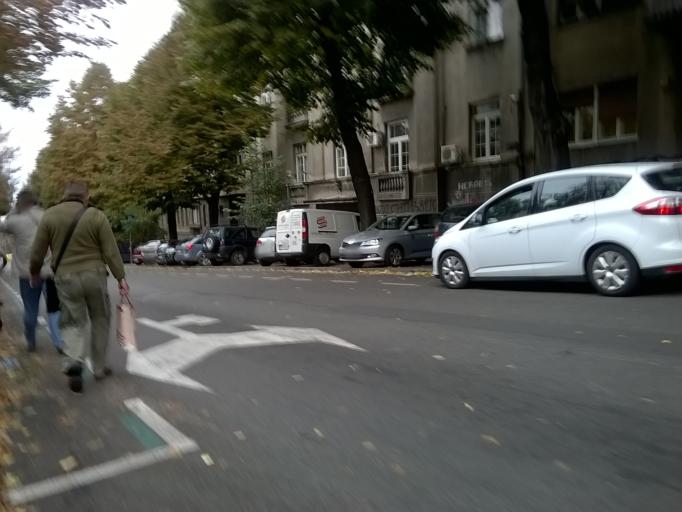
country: RS
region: Central Serbia
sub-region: Belgrade
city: Stari Grad
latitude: 44.8156
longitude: 20.4708
